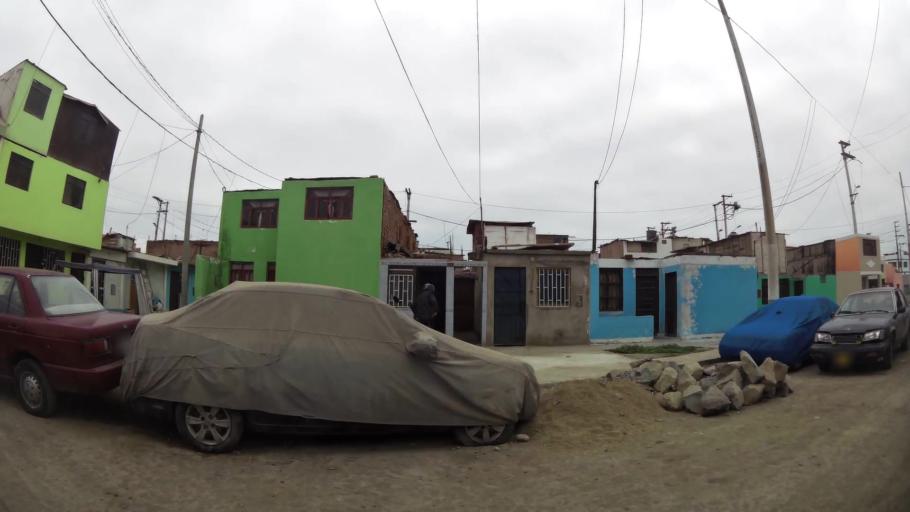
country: PE
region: Callao
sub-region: Callao
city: Callao
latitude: -12.0690
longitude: -77.1340
